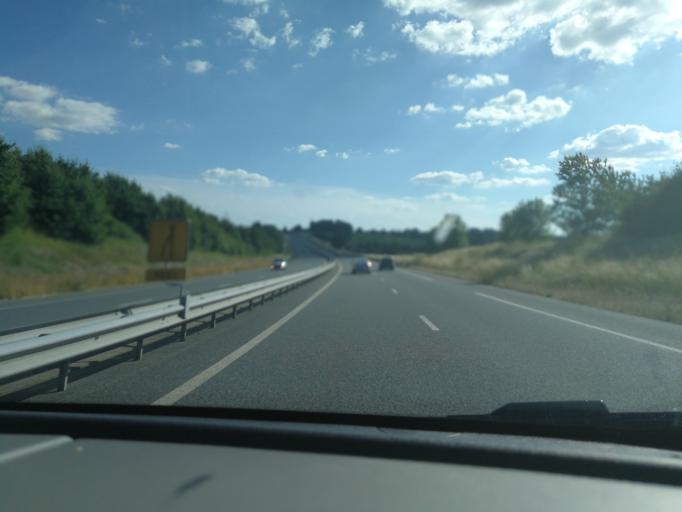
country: FR
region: Midi-Pyrenees
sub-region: Departement de l'Aveyron
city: Luc-la-Primaube
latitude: 44.3051
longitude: 2.5313
